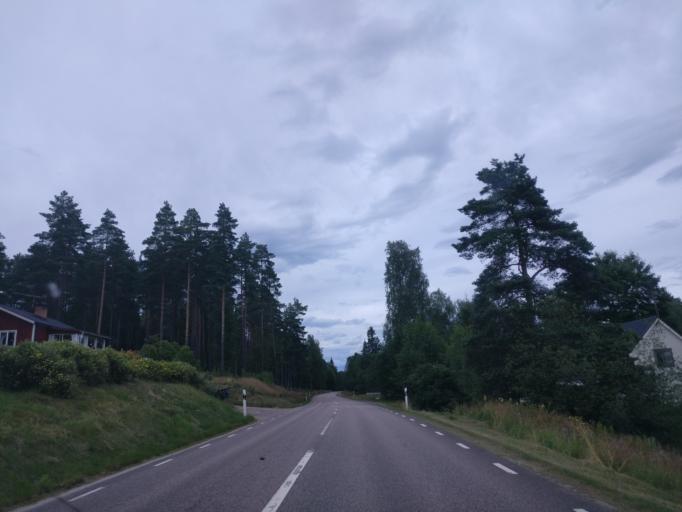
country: SE
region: Vaermland
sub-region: Hagfors Kommun
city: Ekshaerad
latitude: 60.1632
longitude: 13.4755
